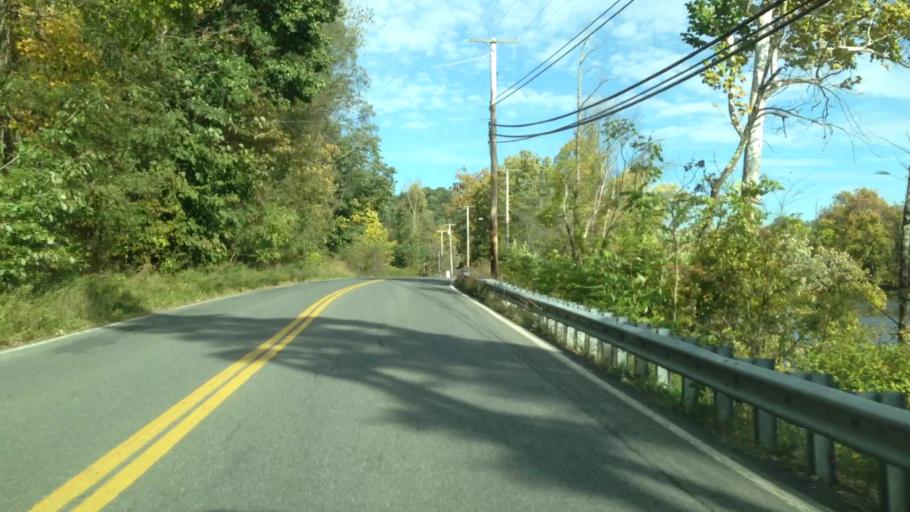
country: US
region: New York
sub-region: Ulster County
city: Kingston
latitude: 41.9036
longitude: -74.0118
